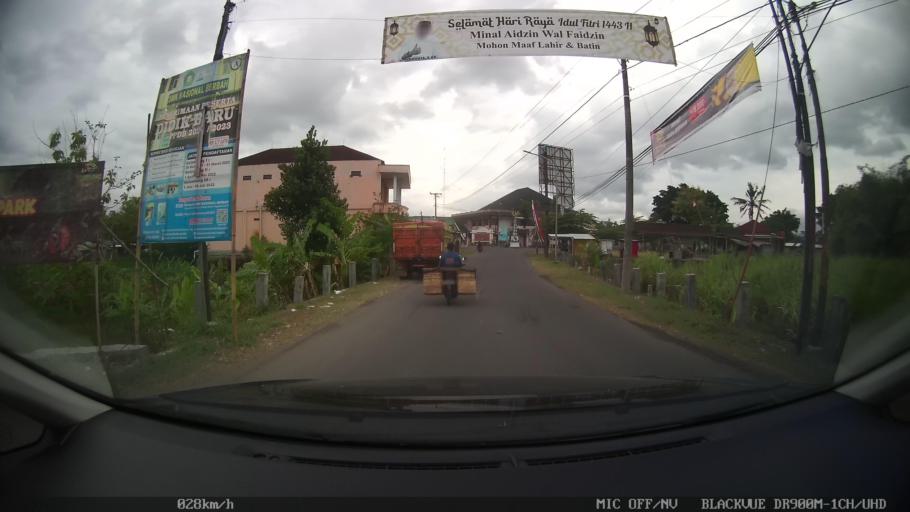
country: ID
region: Daerah Istimewa Yogyakarta
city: Depok
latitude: -7.8341
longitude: 110.4217
